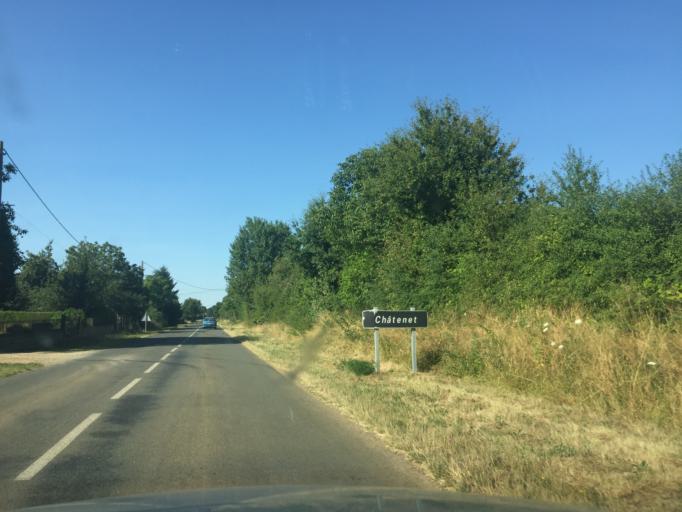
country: FR
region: Poitou-Charentes
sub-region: Departement des Deux-Sevres
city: Lezay
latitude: 46.1985
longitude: -0.0378
